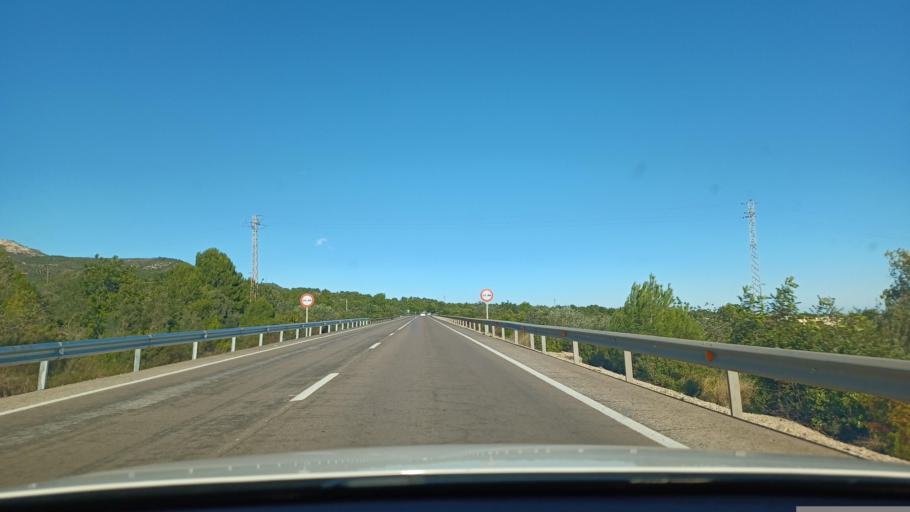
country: ES
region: Catalonia
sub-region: Provincia de Tarragona
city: Sant Carles de la Rapita
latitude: 40.5952
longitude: 0.5551
